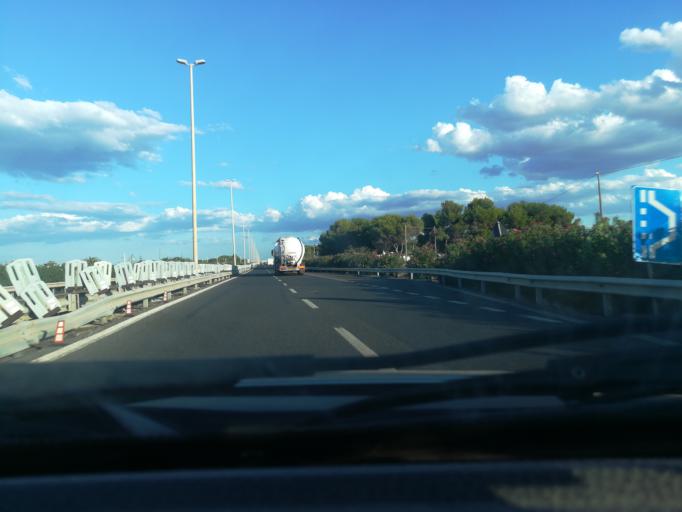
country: IT
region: Apulia
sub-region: Provincia di Bari
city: Mola di Bari
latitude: 41.0764
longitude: 17.0512
